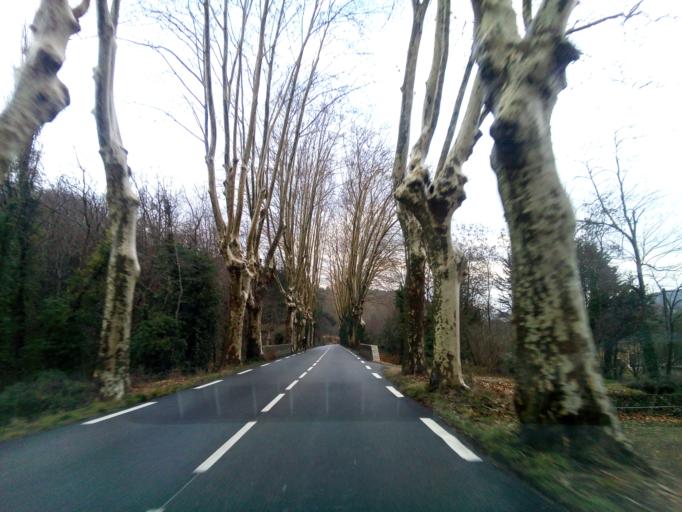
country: FR
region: Rhone-Alpes
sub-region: Departement de l'Ardeche
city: Saint-Laurent-du-Pape
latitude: 44.8236
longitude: 4.7316
